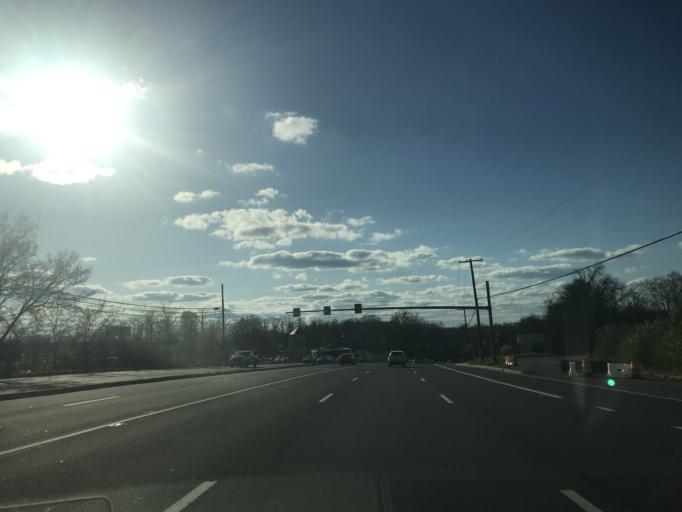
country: US
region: Maryland
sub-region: Prince George's County
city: Glenarden
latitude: 38.9176
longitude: -76.8580
